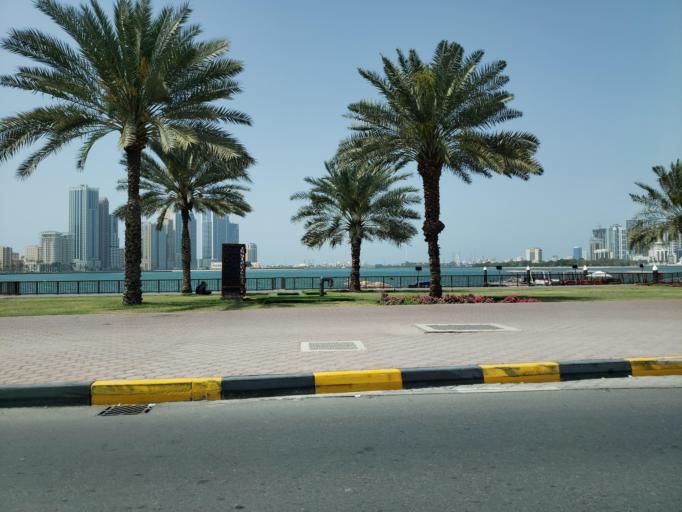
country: AE
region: Ash Shariqah
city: Sharjah
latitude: 25.3247
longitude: 55.3851
